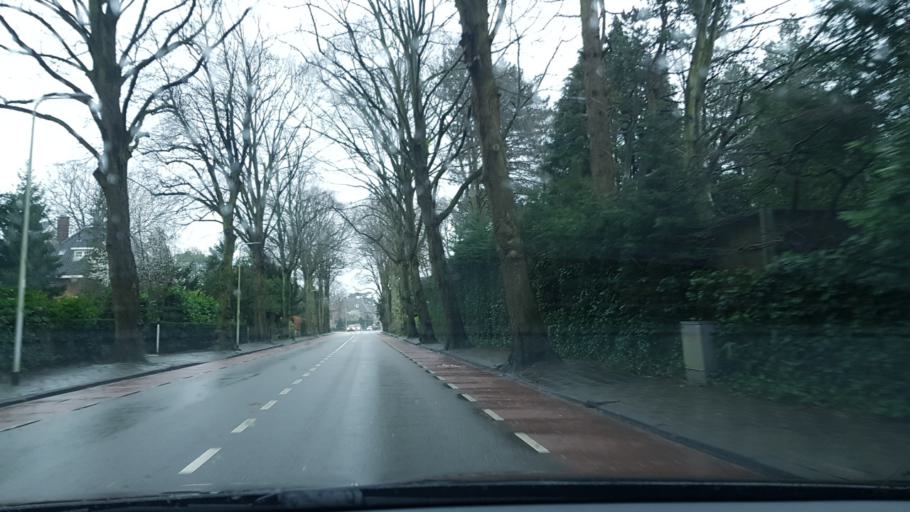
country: NL
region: North Holland
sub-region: Gemeente Heemstede
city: Heemstede
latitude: 52.3660
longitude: 4.5998
